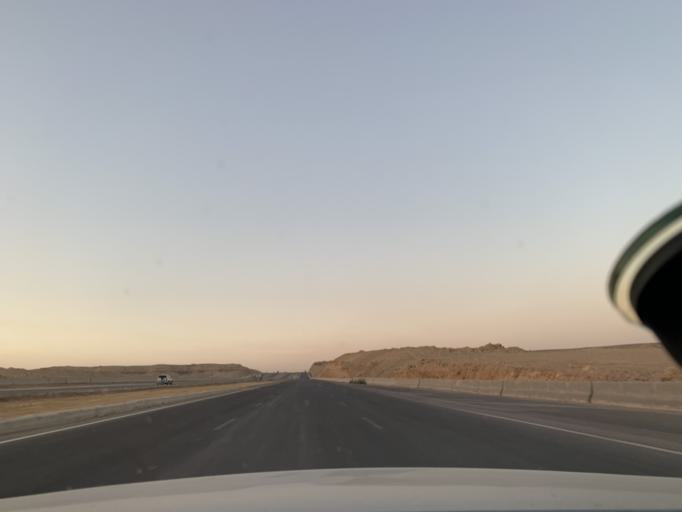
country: EG
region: Muhafazat al Qahirah
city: Halwan
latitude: 29.9421
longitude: 31.5325
